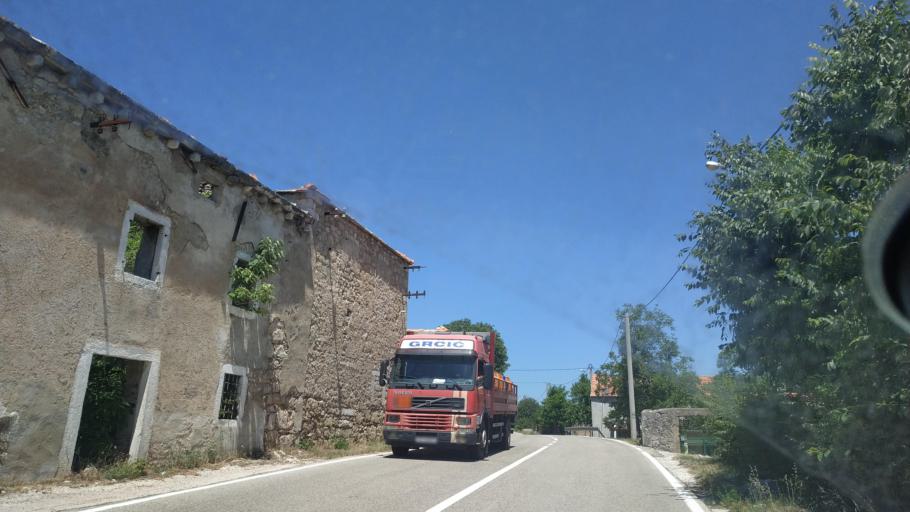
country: HR
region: Sibensko-Kniniska
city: Drnis
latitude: 43.8929
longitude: 16.2096
